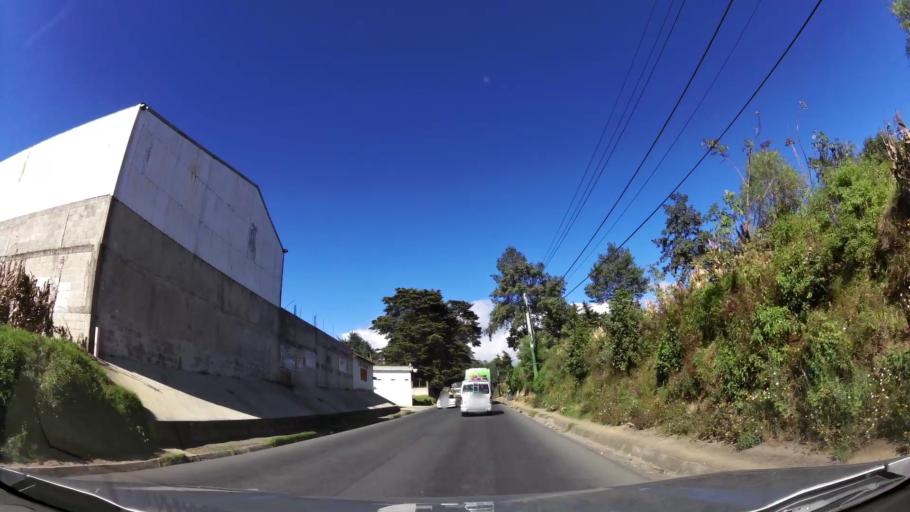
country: GT
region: Solola
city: Solola
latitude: 14.8004
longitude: -91.1801
